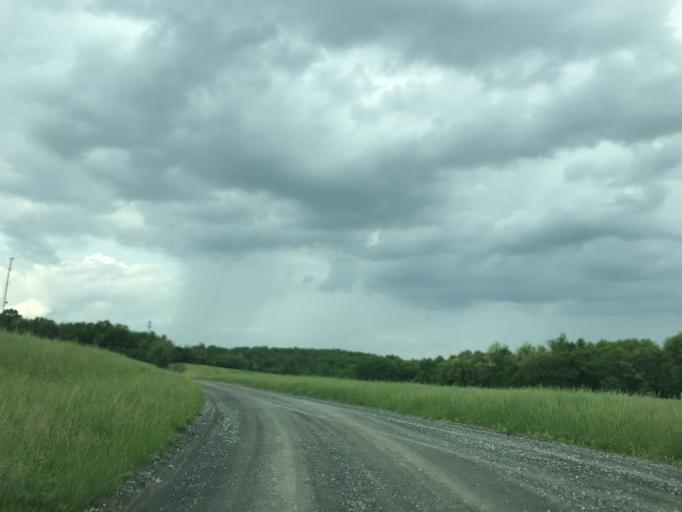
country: US
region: Pennsylvania
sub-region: York County
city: Susquehanna Trails
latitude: 39.6997
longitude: -76.3439
